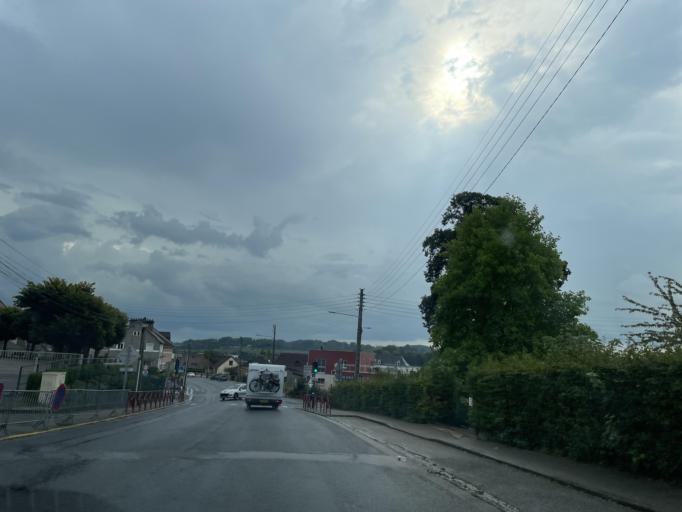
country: FR
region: Haute-Normandie
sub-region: Departement de la Seine-Maritime
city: Neufchatel-en-Bray
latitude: 49.7365
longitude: 1.4373
